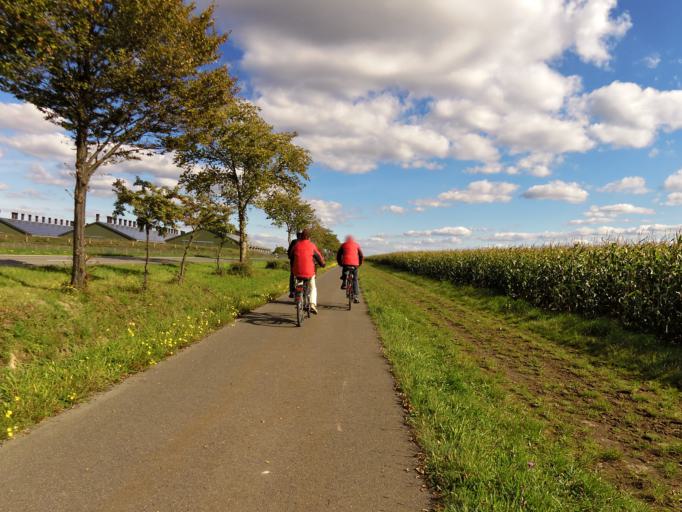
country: DE
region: North Rhine-Westphalia
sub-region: Regierungsbezirk Koln
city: Rheinbach
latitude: 50.6288
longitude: 6.8803
